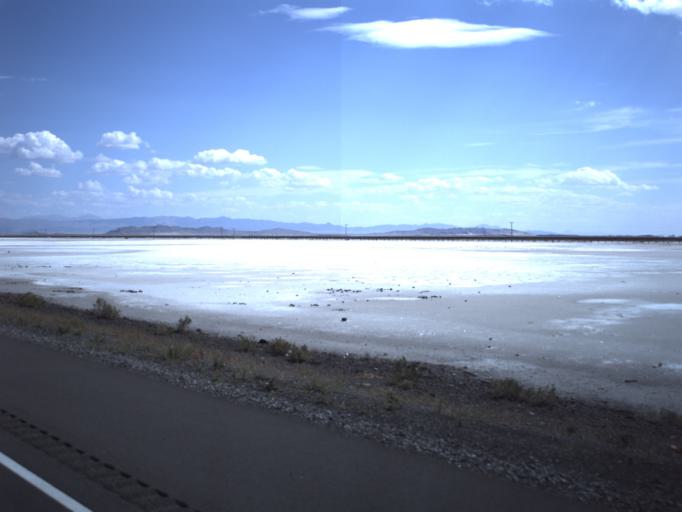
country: US
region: Utah
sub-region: Tooele County
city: Wendover
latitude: 40.7292
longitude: -113.4263
